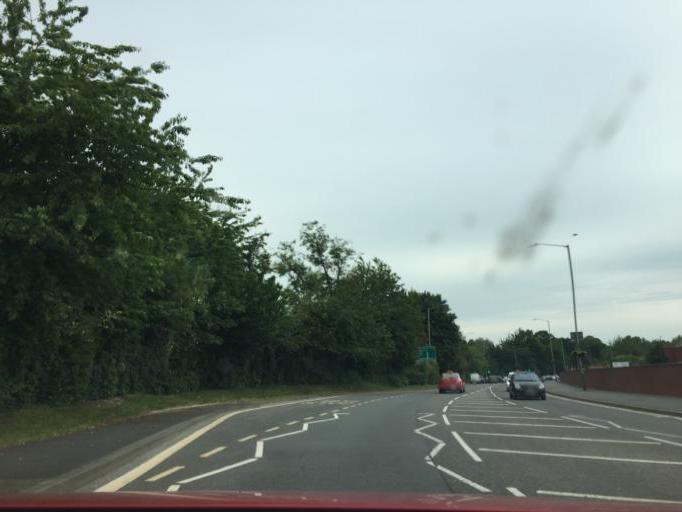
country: GB
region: England
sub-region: Warwickshire
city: Nuneaton
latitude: 52.5210
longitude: -1.4708
